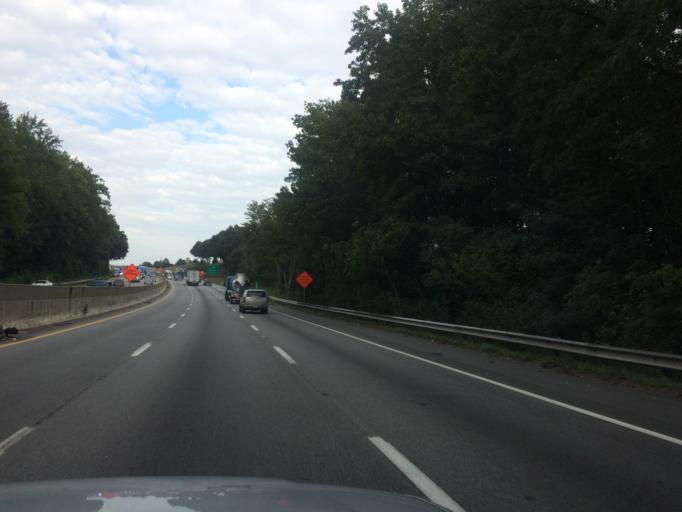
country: US
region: South Carolina
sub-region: Greenville County
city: Mauldin
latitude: 34.8168
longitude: -82.3247
